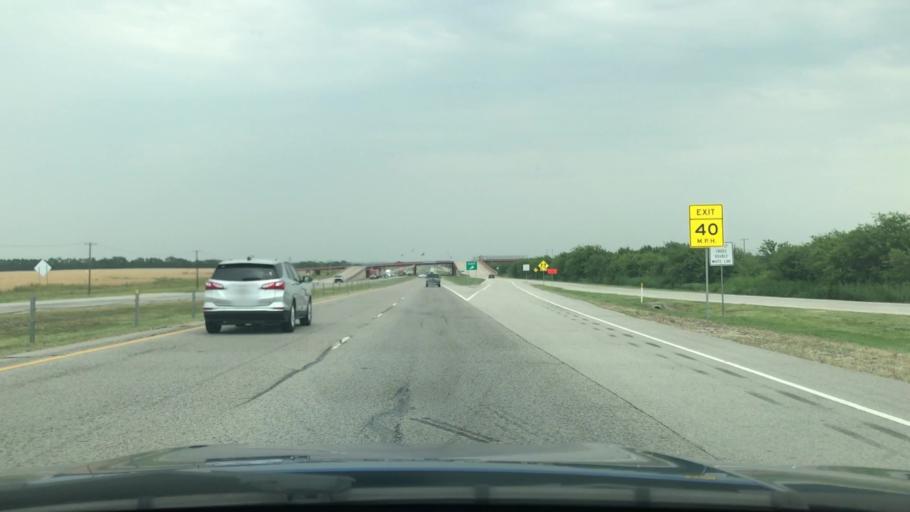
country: US
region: Texas
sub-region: Kaufman County
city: Forney
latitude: 32.7406
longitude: -96.4200
